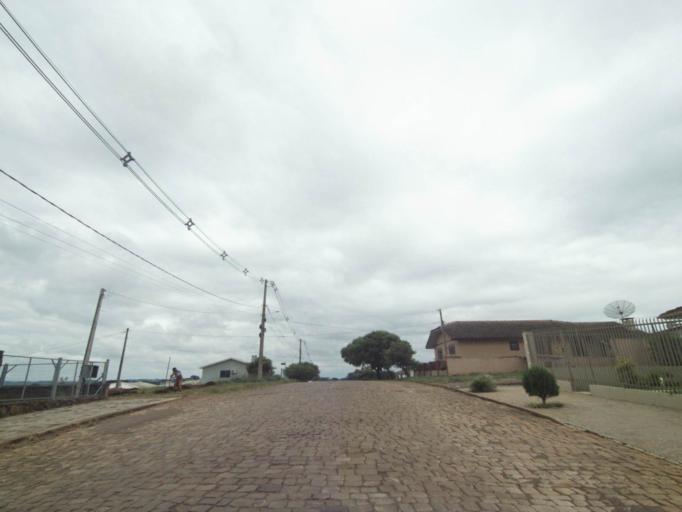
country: BR
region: Rio Grande do Sul
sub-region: Lagoa Vermelha
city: Lagoa Vermelha
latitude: -28.2179
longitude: -51.5332
